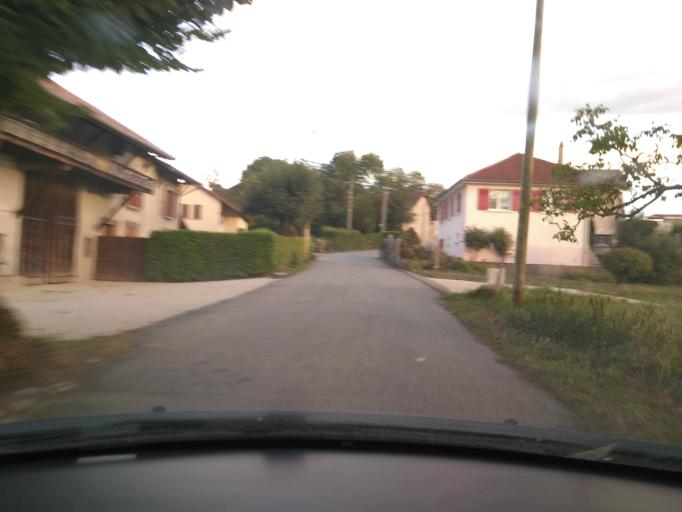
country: FR
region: Rhone-Alpes
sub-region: Departement de l'Isere
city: La Murette
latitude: 45.3821
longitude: 5.5173
